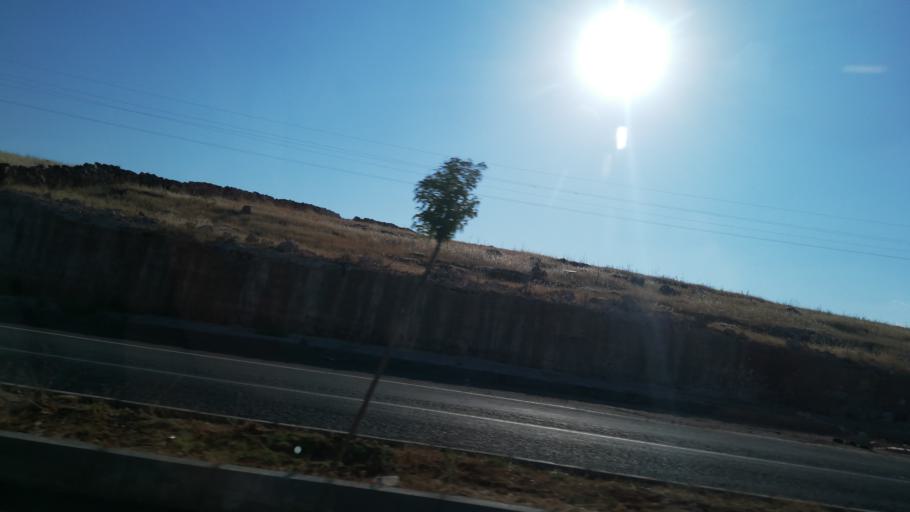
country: TR
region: Mardin
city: Midyat
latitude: 37.3997
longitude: 41.3441
